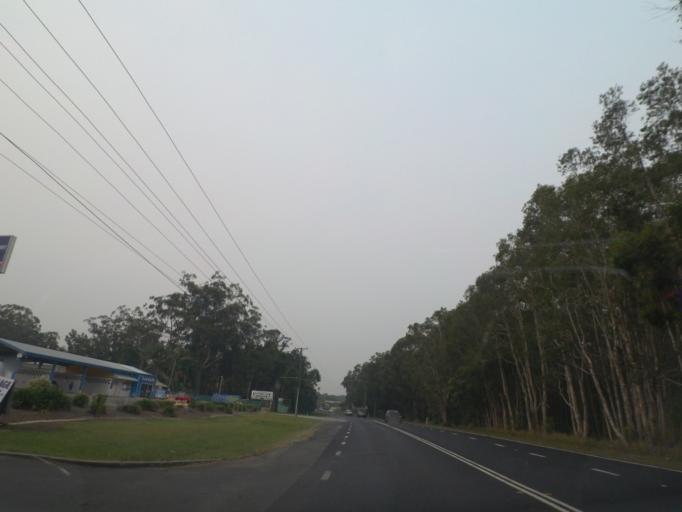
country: AU
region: New South Wales
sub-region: Coffs Harbour
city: Toormina
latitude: -30.3490
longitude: 153.0917
